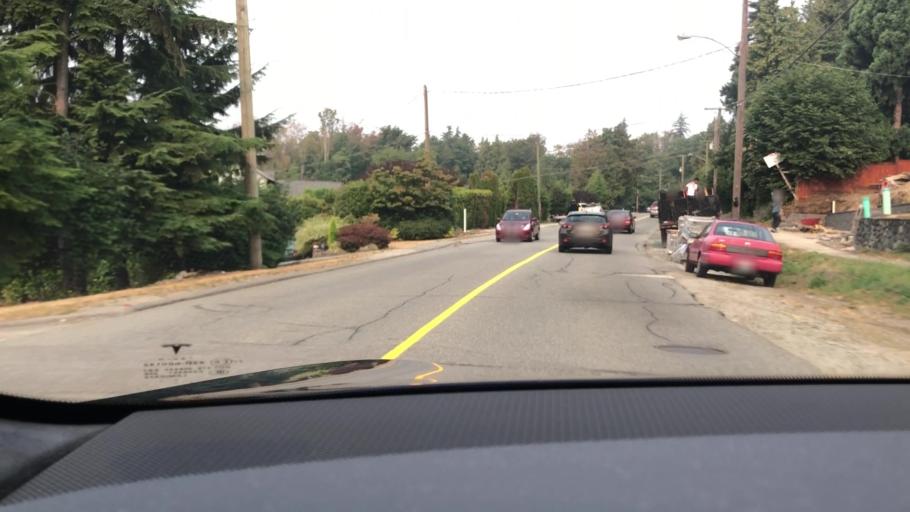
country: CA
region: British Columbia
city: Burnaby
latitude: 49.2083
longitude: -123.0018
